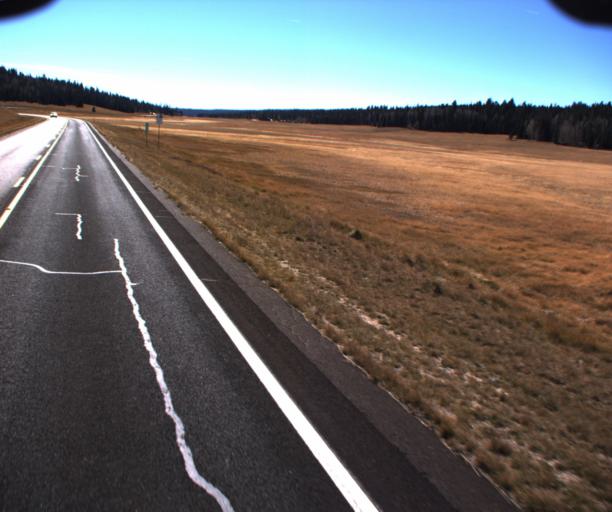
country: US
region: Arizona
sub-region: Coconino County
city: Grand Canyon
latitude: 36.4272
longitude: -112.1317
